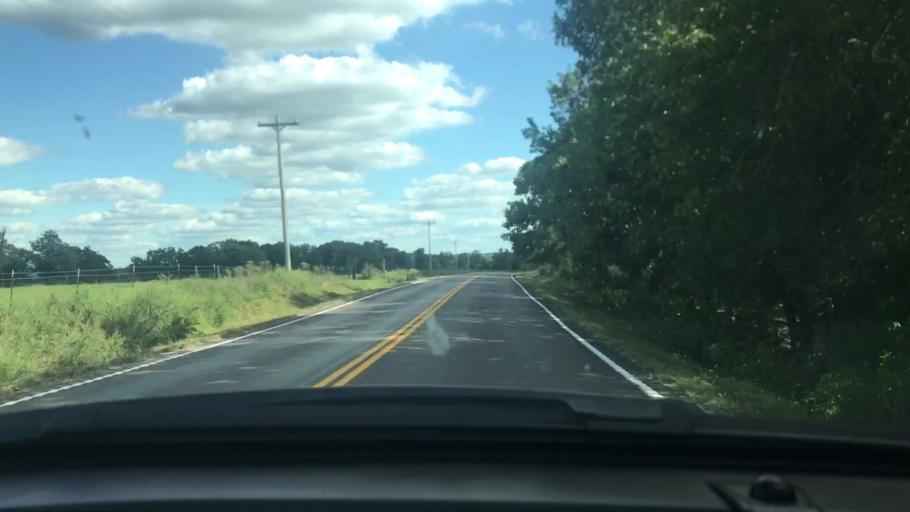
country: US
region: Missouri
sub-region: Wright County
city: Mountain Grove
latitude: 37.2976
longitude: -92.3107
